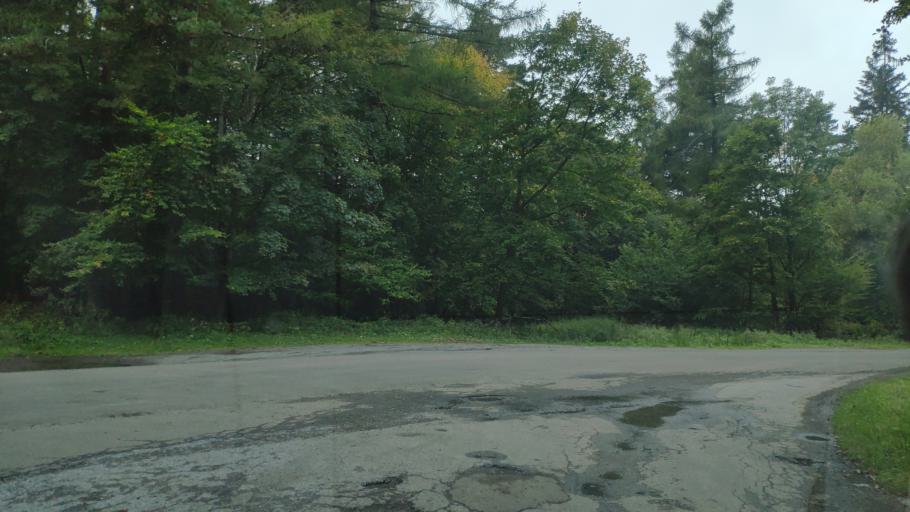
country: SK
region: Presovsky
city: Giraltovce
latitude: 48.9194
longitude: 21.4524
